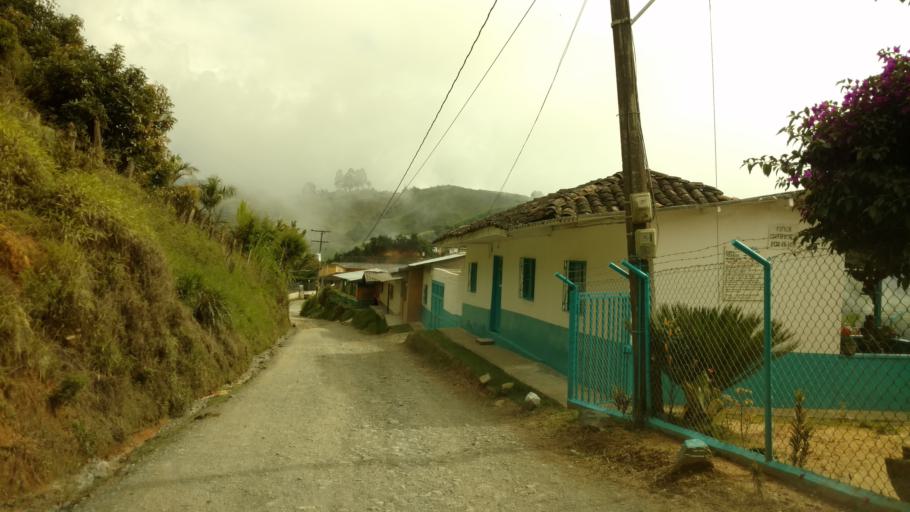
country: CO
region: Caldas
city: Aguadas
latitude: 5.6278
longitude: -75.4524
